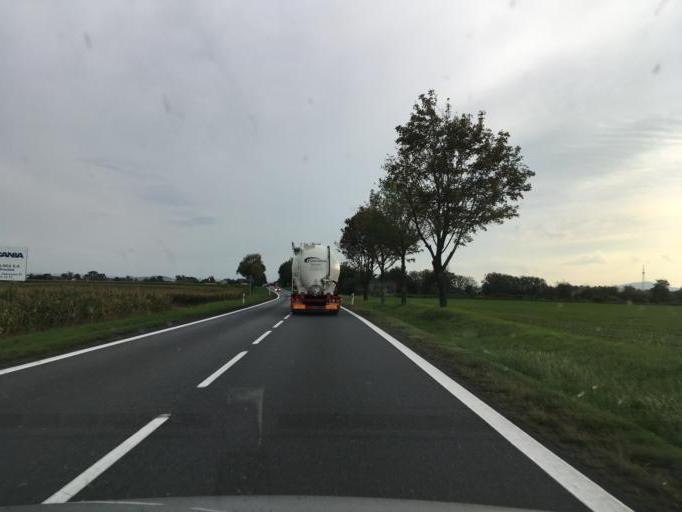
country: PL
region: Lower Silesian Voivodeship
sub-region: Powiat wroclawski
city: Jordanow Slaski
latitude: 50.9102
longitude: 16.8864
